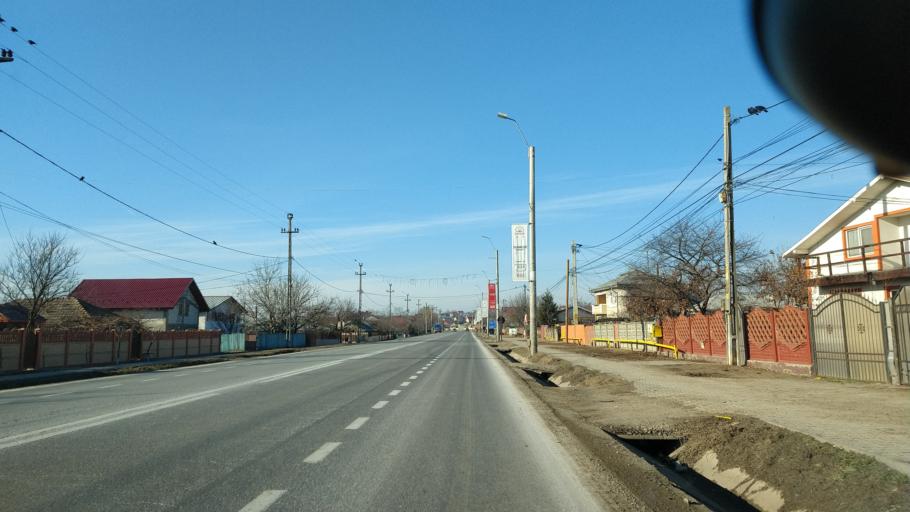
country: RO
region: Iasi
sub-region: Comuna Letcani
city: Letcani
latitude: 47.1932
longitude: 27.4219
